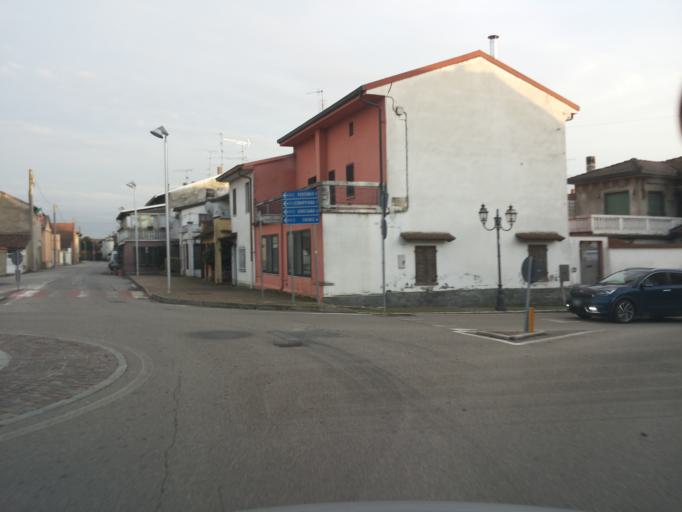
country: IT
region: Piedmont
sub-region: Provincia di Vercelli
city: Costanzana
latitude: 45.2376
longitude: 8.3708
